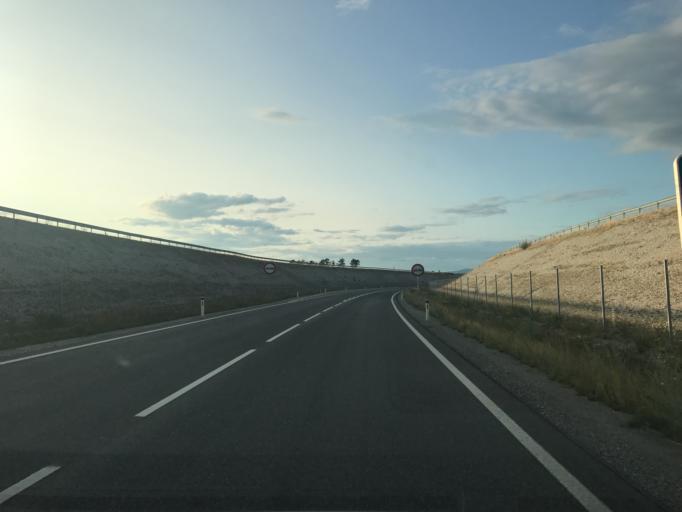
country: AT
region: Lower Austria
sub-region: Politischer Bezirk Wiener Neustadt
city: Sollenau
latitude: 47.8661
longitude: 16.2717
